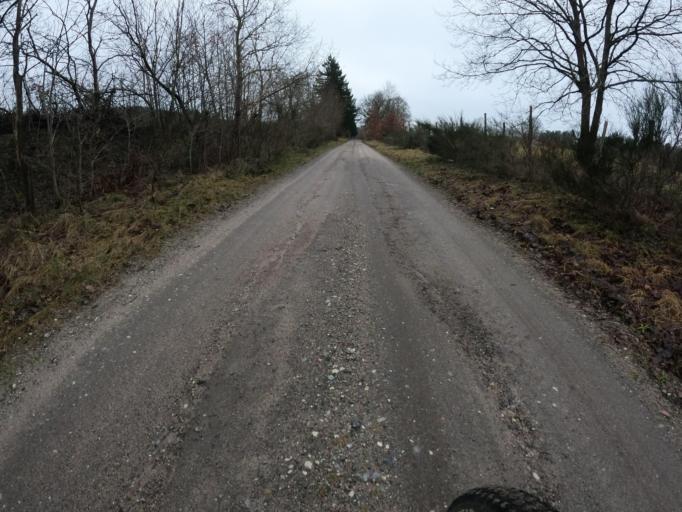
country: PL
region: West Pomeranian Voivodeship
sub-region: Powiat koszalinski
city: Polanow
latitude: 54.2388
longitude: 16.6442
